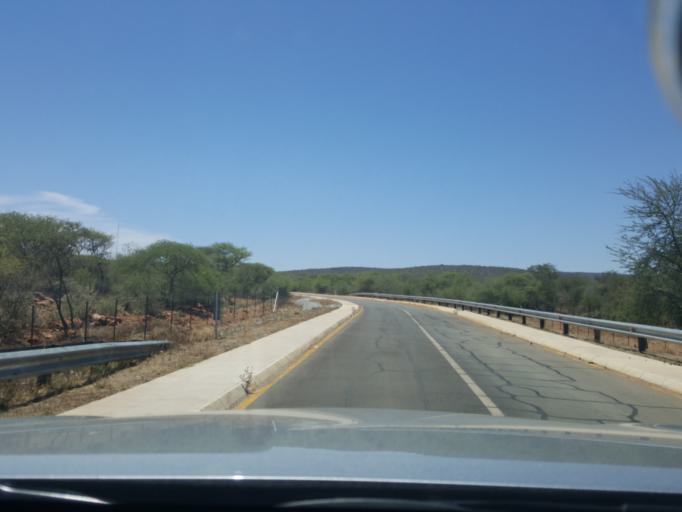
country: BW
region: South East
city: Ramotswa
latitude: -24.8726
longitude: 25.8836
